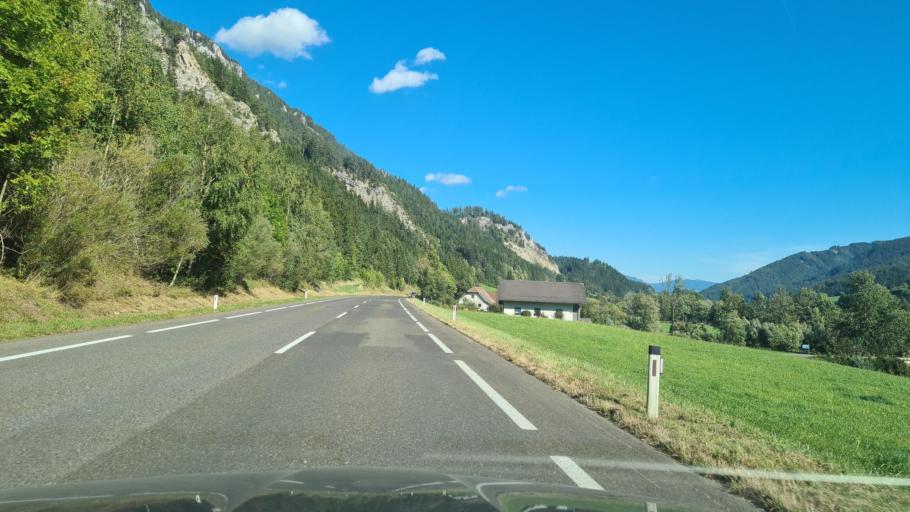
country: AT
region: Styria
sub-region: Politischer Bezirk Leoben
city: Mautern in Steiermark
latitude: 47.3974
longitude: 14.8487
